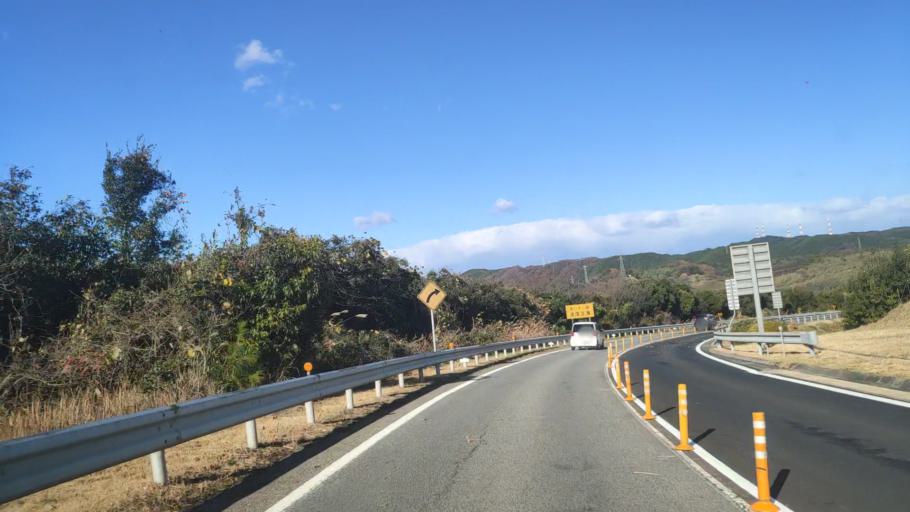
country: JP
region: Ehime
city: Saijo
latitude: 33.9153
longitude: 133.2368
